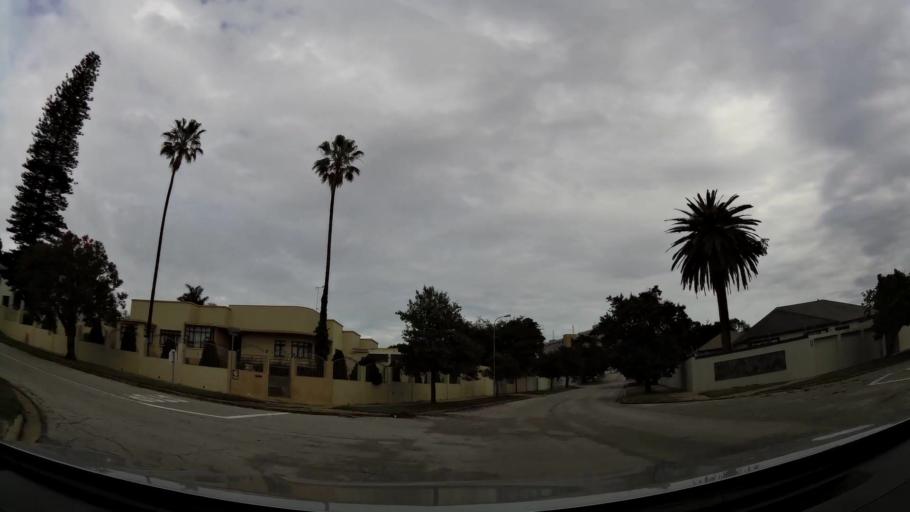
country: ZA
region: Eastern Cape
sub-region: Nelson Mandela Bay Metropolitan Municipality
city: Port Elizabeth
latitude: -33.9542
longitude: 25.5993
